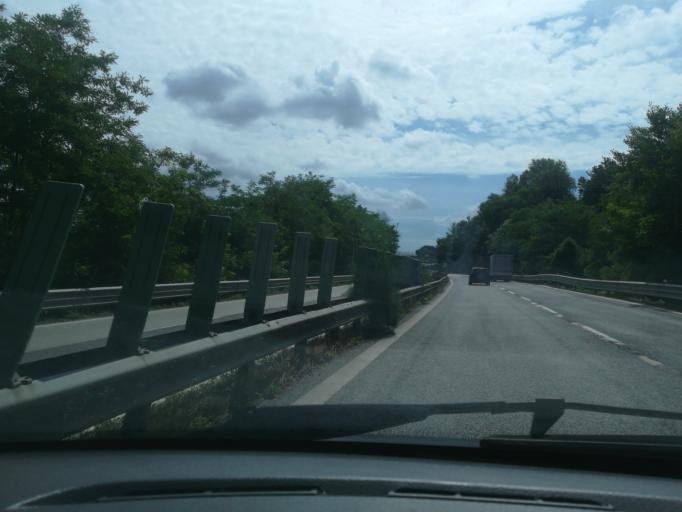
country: IT
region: The Marches
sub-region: Provincia di Macerata
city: Corridonia
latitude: 43.2651
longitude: 13.5296
